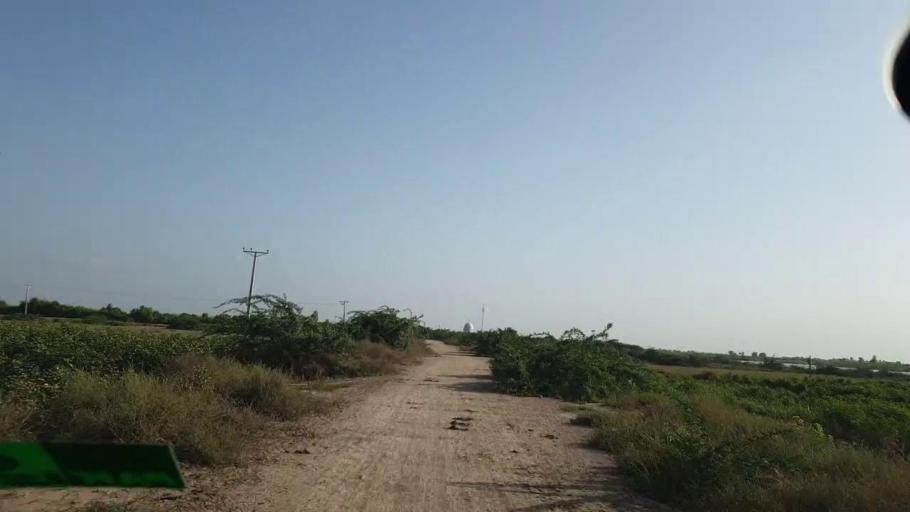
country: PK
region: Sindh
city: Naukot
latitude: 24.7383
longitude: 69.2477
